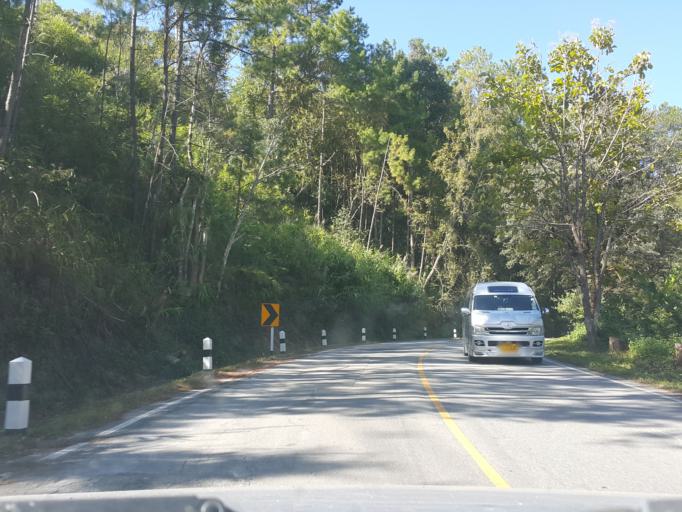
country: TH
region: Mae Hong Son
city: Mae Hi
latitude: 19.2702
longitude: 98.5783
